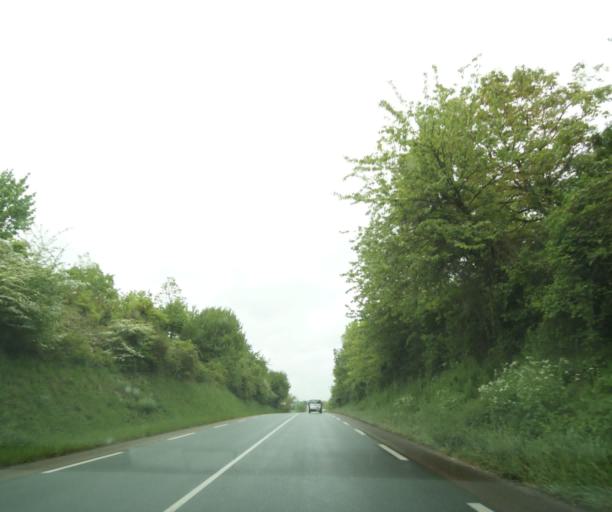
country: FR
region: Poitou-Charentes
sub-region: Departement de la Charente-Maritime
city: Les Gonds
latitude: 45.6786
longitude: -0.6064
